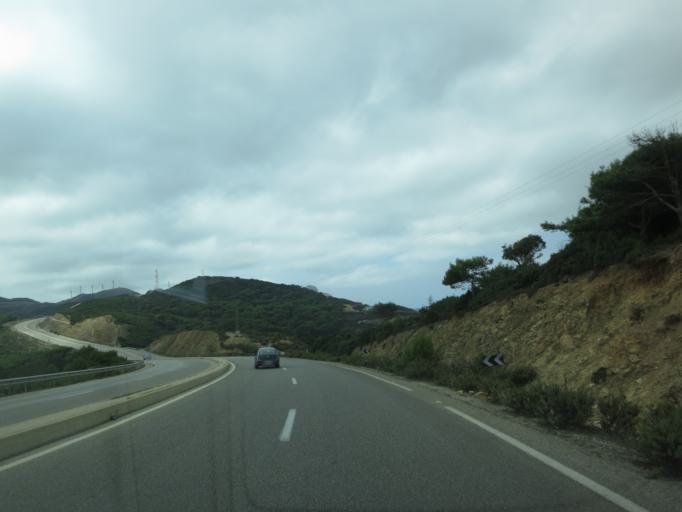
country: ES
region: Ceuta
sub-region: Ceuta
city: Ceuta
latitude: 35.8641
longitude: -5.4188
